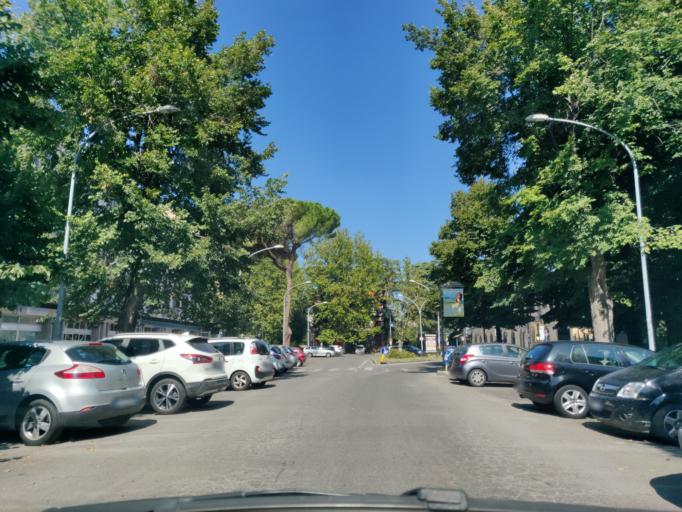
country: IT
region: Latium
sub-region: Provincia di Viterbo
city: Viterbo
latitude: 42.4244
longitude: 12.1061
